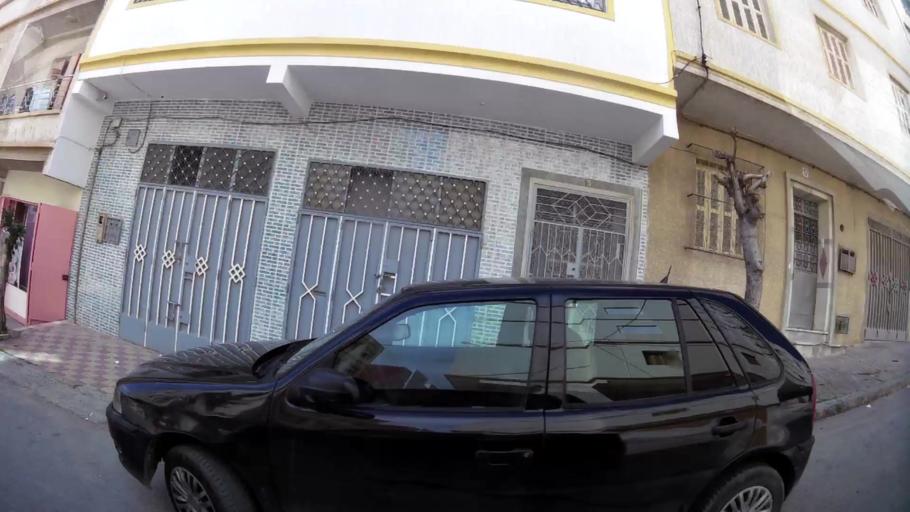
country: MA
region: Tanger-Tetouan
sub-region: Tanger-Assilah
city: Tangier
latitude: 35.7550
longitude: -5.8055
